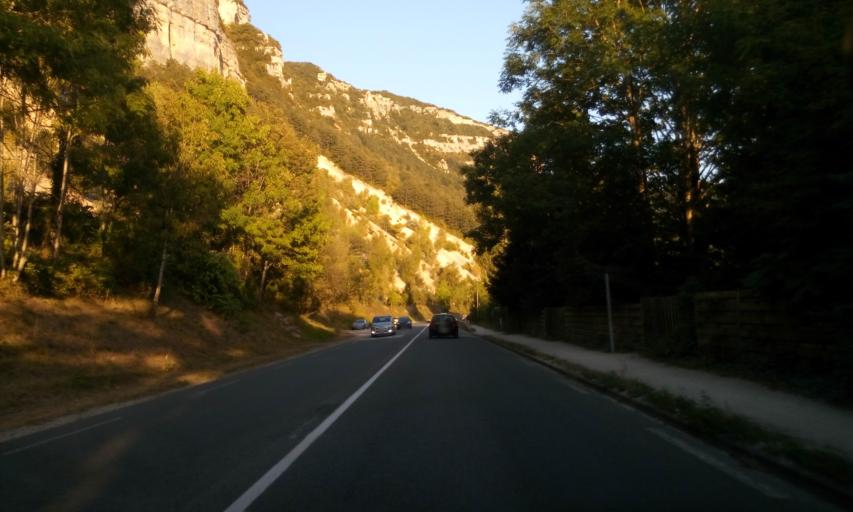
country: FR
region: Rhone-Alpes
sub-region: Departement de l'Ain
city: Montreal-la-Cluse
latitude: 46.1630
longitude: 5.5940
